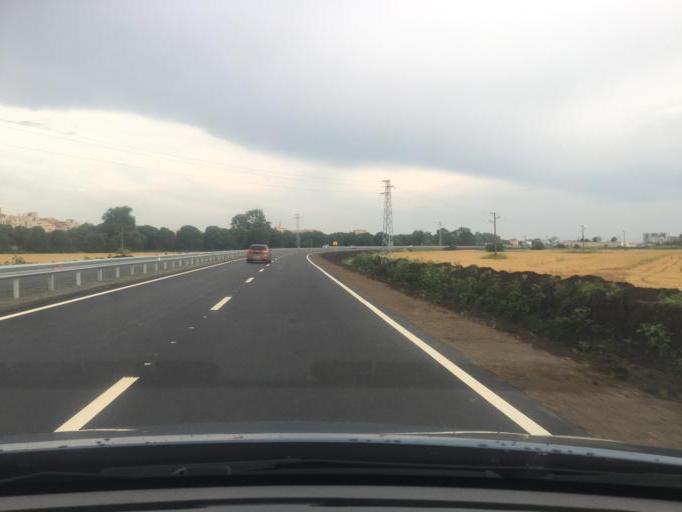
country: BG
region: Burgas
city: Aheloy
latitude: 42.6419
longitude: 27.6382
